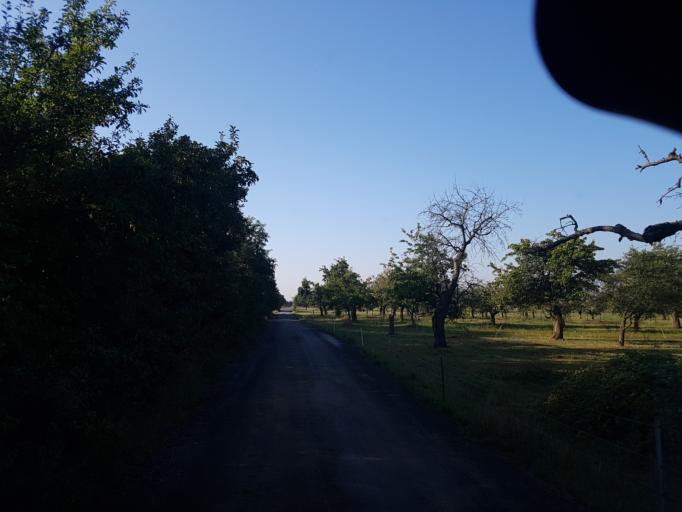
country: DE
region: Brandenburg
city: Hohenleipisch
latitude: 51.5013
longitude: 13.5489
